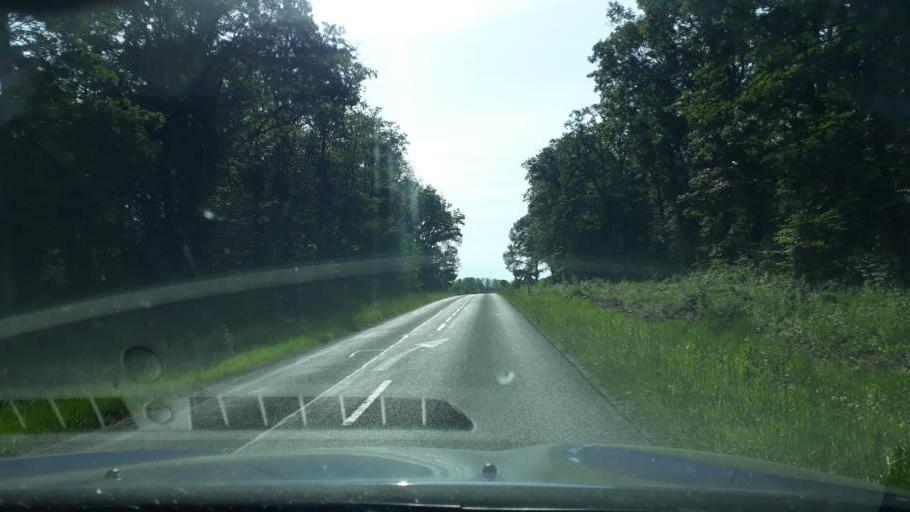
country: FR
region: Centre
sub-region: Departement du Loiret
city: Boynes
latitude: 48.0563
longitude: 2.2821
